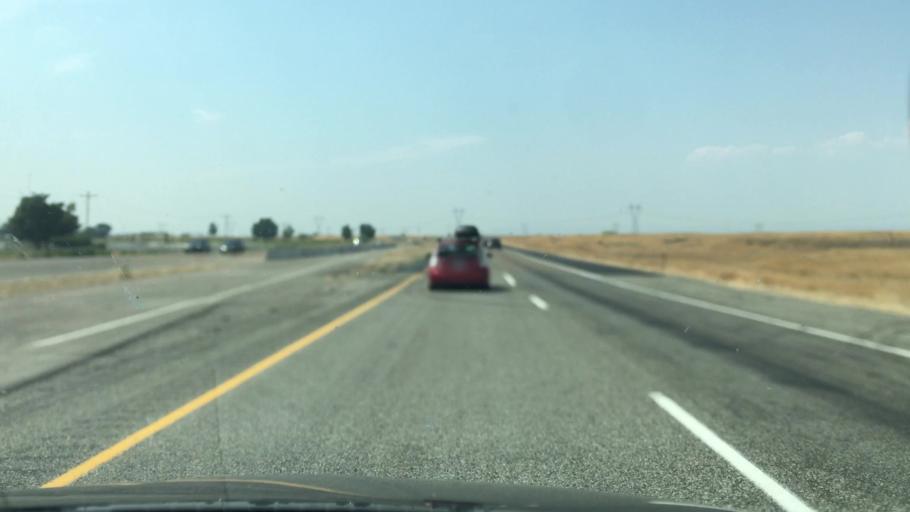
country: US
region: Idaho
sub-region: Gooding County
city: Wendell
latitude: 42.8322
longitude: -114.8092
